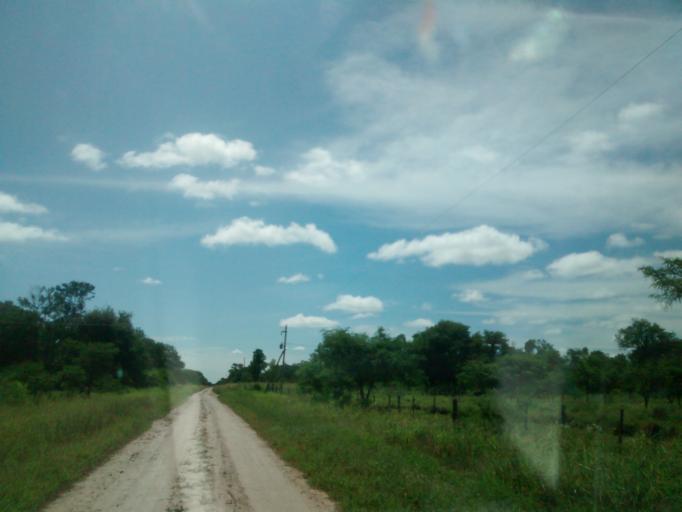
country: AR
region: Chaco
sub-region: Departamento de Quitilipi
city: Quitilipi
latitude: -26.7818
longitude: -60.2280
